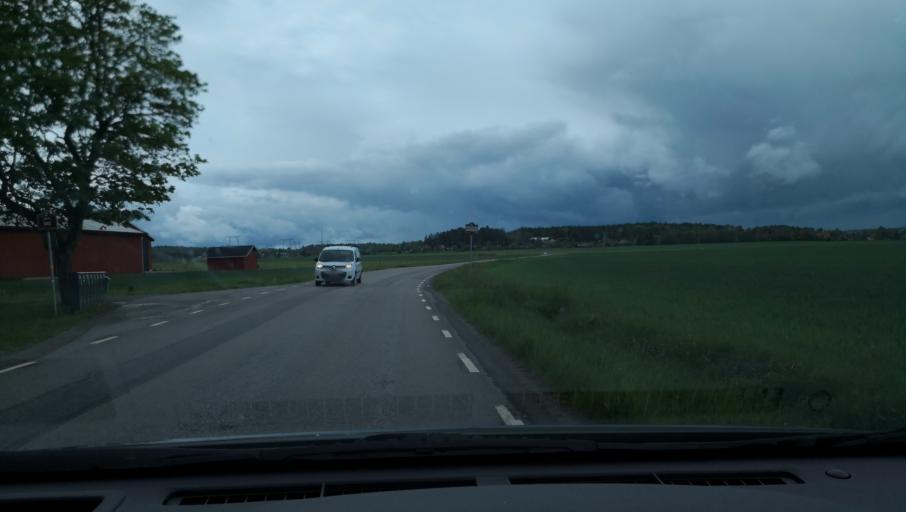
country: SE
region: Uppsala
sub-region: Enkopings Kommun
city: Orsundsbro
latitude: 59.7243
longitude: 17.3164
